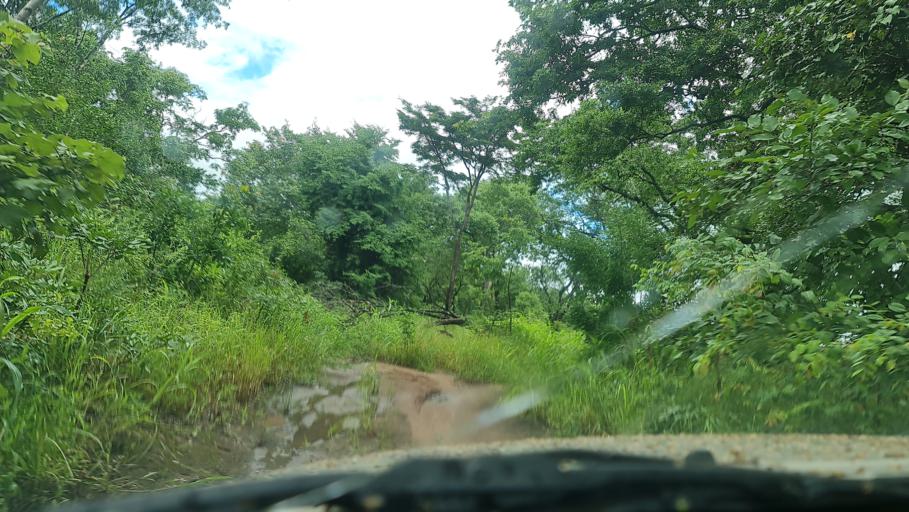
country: MW
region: Southern Region
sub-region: Nsanje District
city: Nsanje
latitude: -17.4481
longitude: 35.8409
